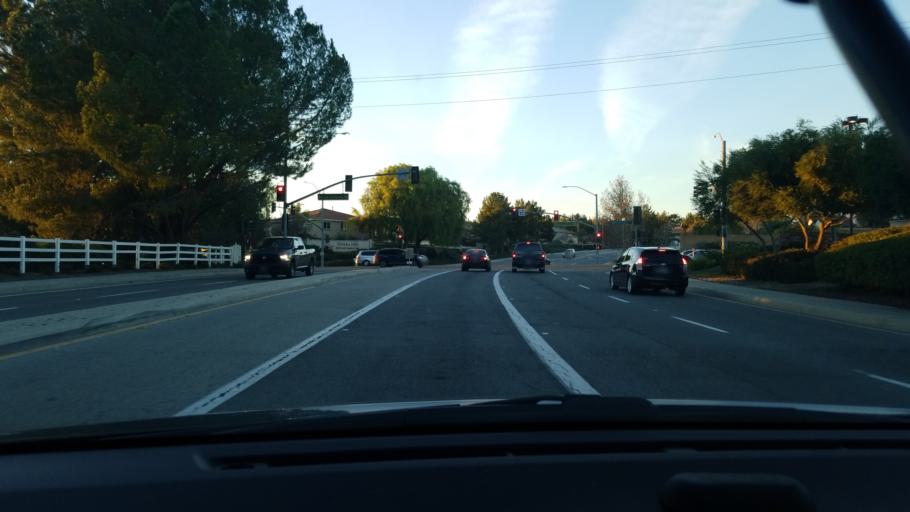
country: US
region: California
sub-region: Riverside County
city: Temecula
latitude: 33.5136
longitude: -117.1043
